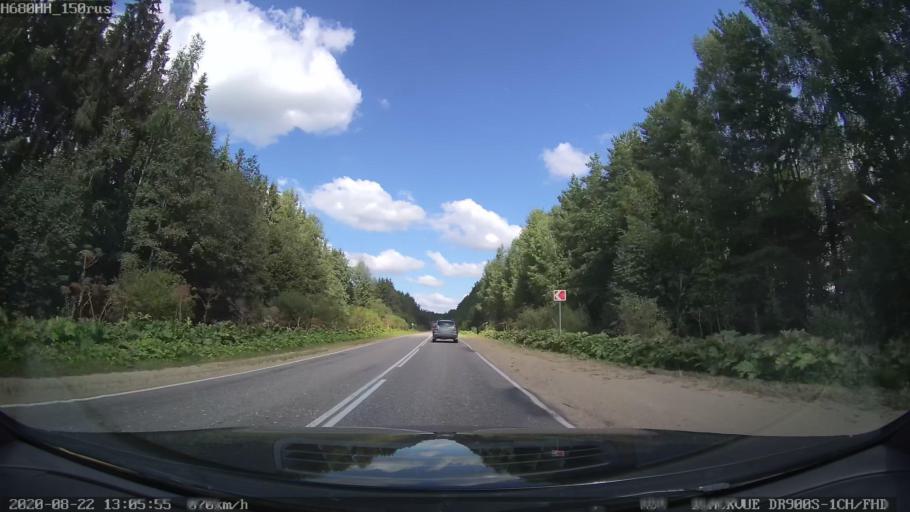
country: RU
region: Tverskaya
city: Bezhetsk
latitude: 57.6761
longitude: 36.4542
